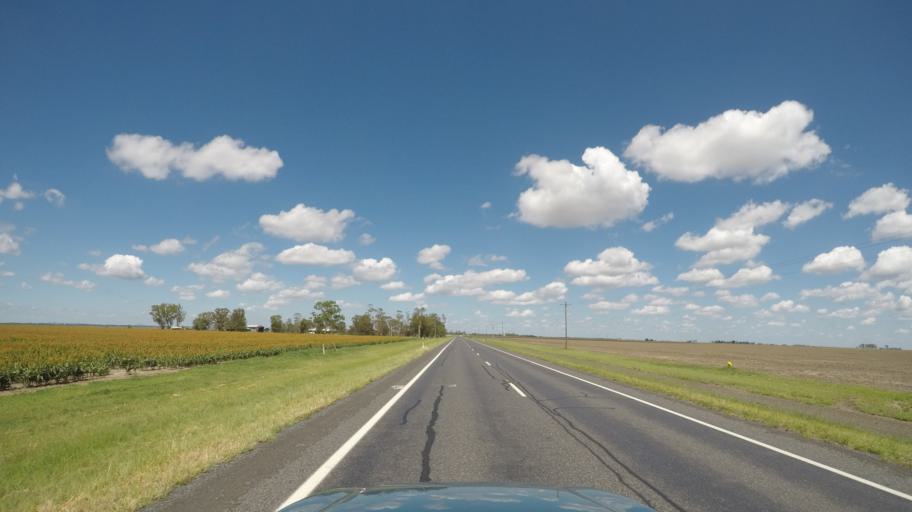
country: AU
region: Queensland
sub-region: Toowoomba
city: Oakey
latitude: -27.7577
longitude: 151.4891
